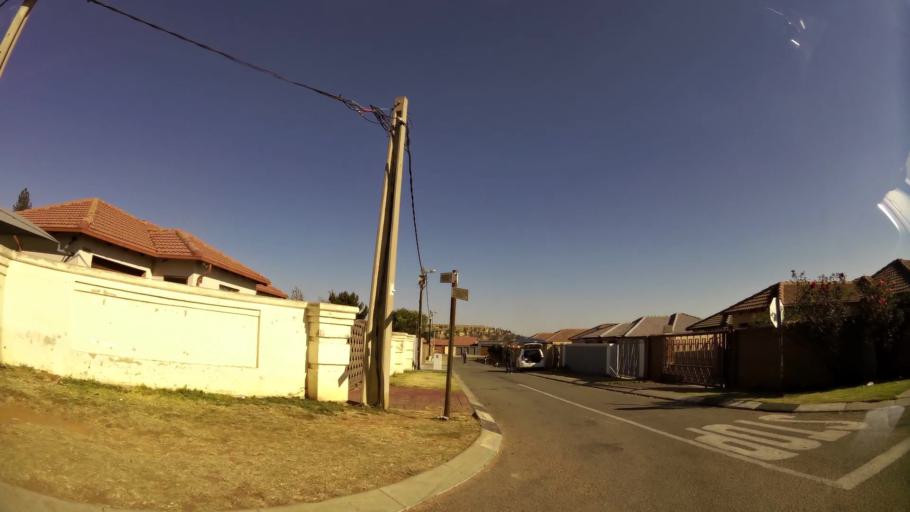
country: ZA
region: Gauteng
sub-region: City of Johannesburg Metropolitan Municipality
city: Johannesburg
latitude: -26.2091
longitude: 27.9777
